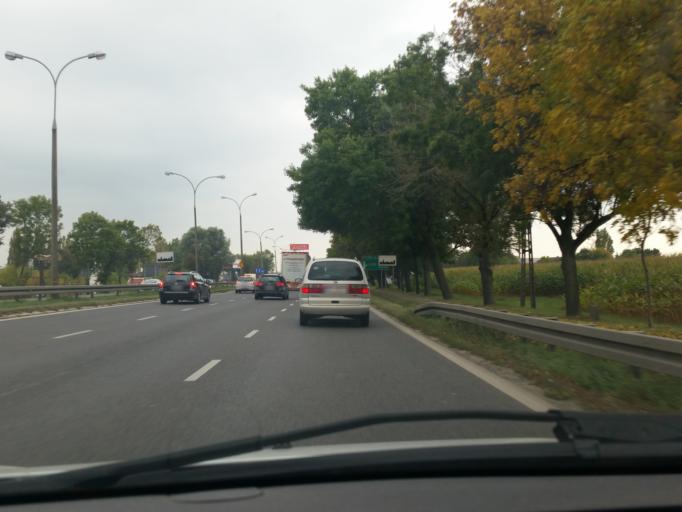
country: PL
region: Masovian Voivodeship
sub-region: Powiat pruszkowski
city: Nowe Grocholice
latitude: 52.1409
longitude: 20.9038
